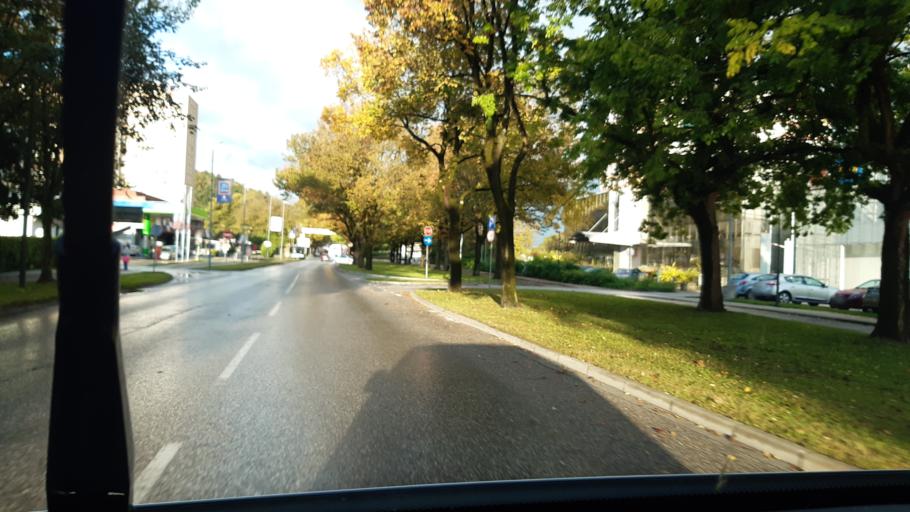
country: SI
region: Ljubljana
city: Ljubljana
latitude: 46.0476
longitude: 14.5473
